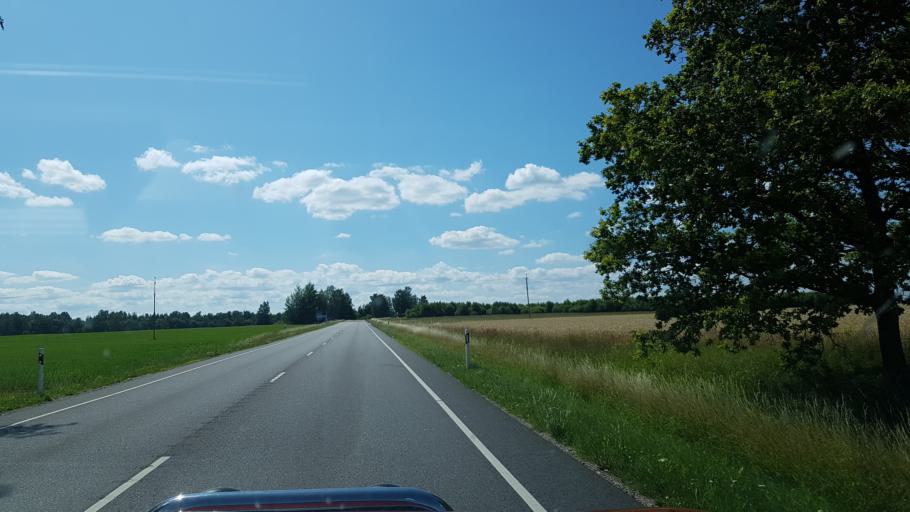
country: EE
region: Viljandimaa
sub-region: Abja vald
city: Abja-Paluoja
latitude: 58.1193
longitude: 25.4388
